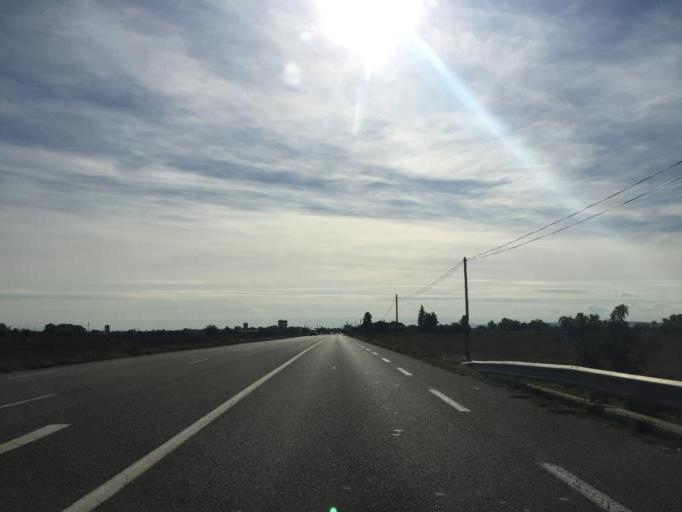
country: FR
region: Rhone-Alpes
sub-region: Departement de la Drome
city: Pierrelatte
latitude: 44.4022
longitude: 4.7057
